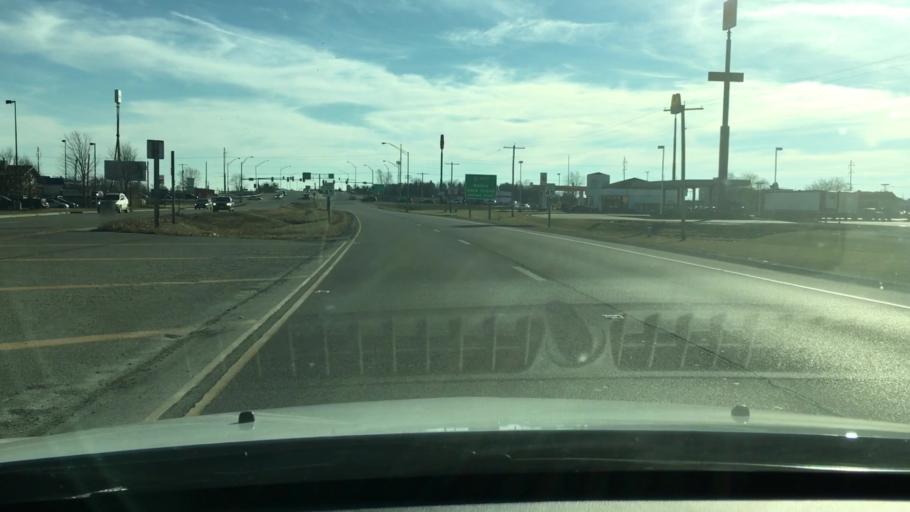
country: US
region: Illinois
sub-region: LaSalle County
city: Peru
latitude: 41.3707
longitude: -89.1257
